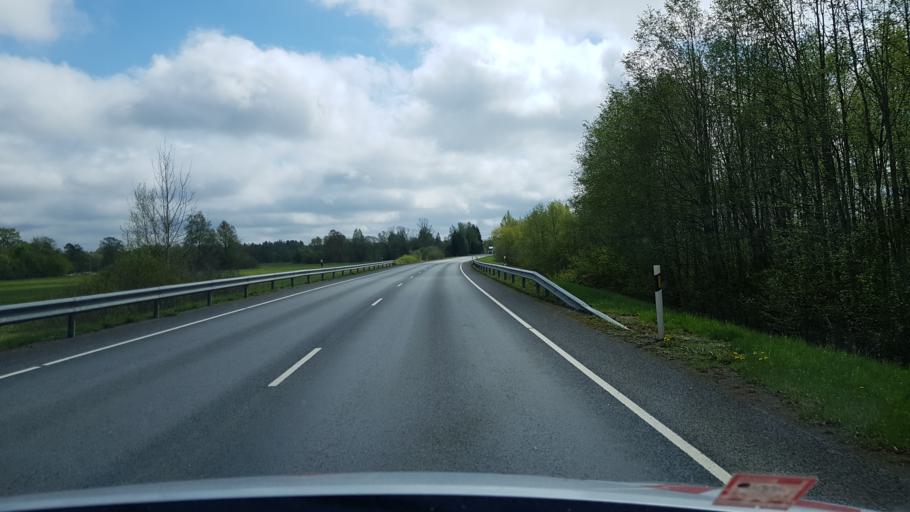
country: EE
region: Paernumaa
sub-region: Saarde vald
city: Kilingi-Nomme
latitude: 58.1894
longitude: 24.7802
